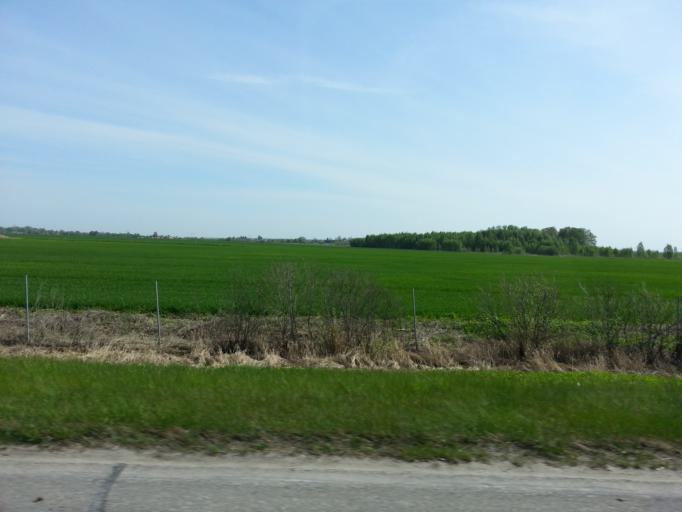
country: LT
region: Panevezys
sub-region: Panevezys City
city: Panevezys
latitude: 55.6200
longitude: 24.4121
